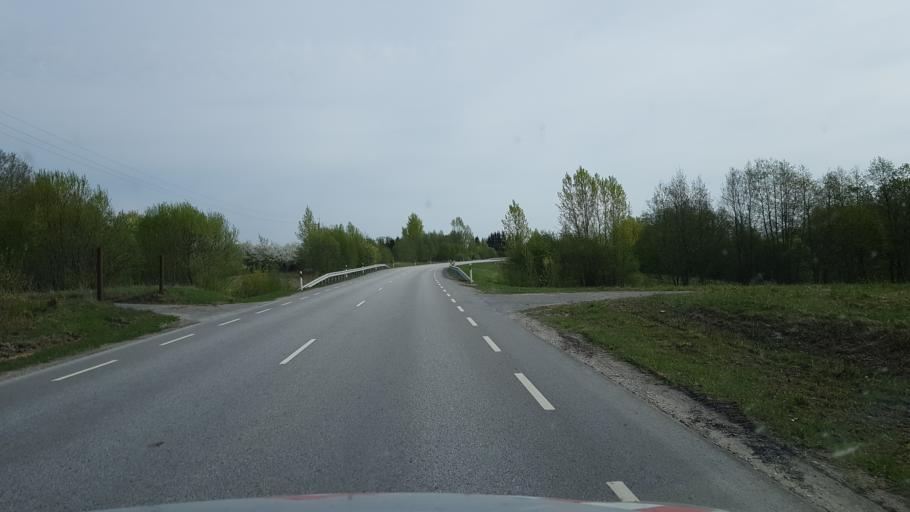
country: EE
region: Paernumaa
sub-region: Sauga vald
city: Sauga
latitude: 58.4424
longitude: 24.4670
